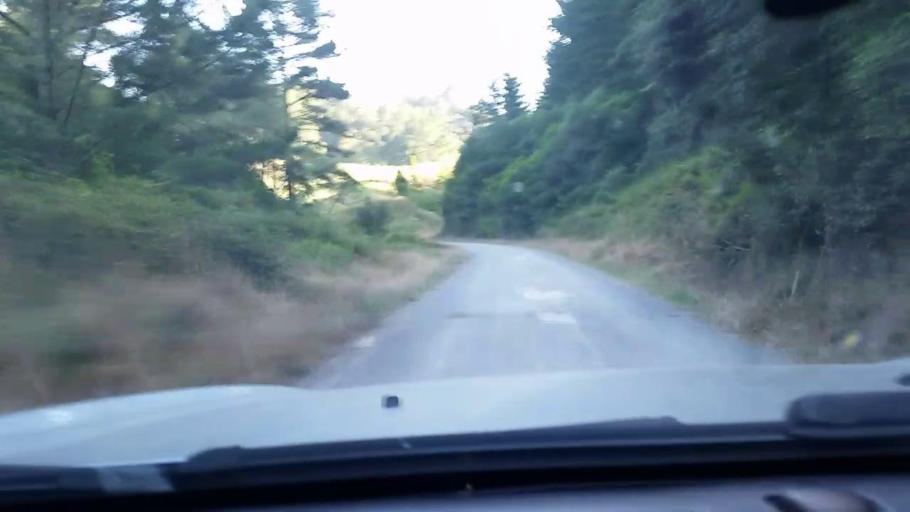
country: NZ
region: Waikato
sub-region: Taupo District
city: Taupo
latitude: -38.4776
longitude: 176.1704
